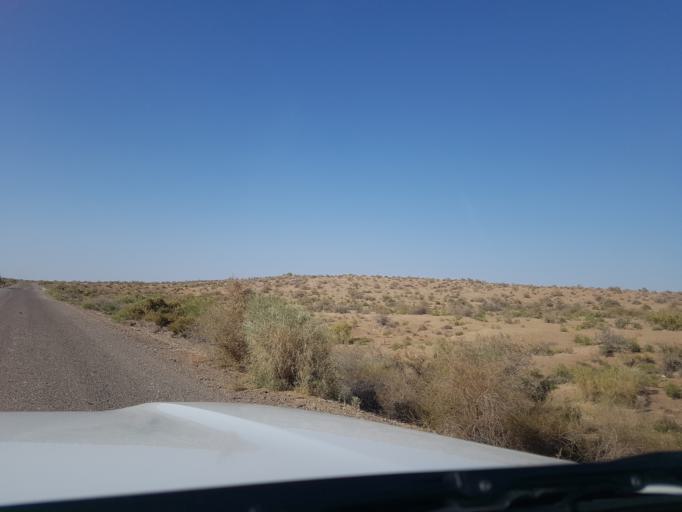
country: IR
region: Razavi Khorasan
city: Sarakhs
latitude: 36.7618
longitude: 61.3259
